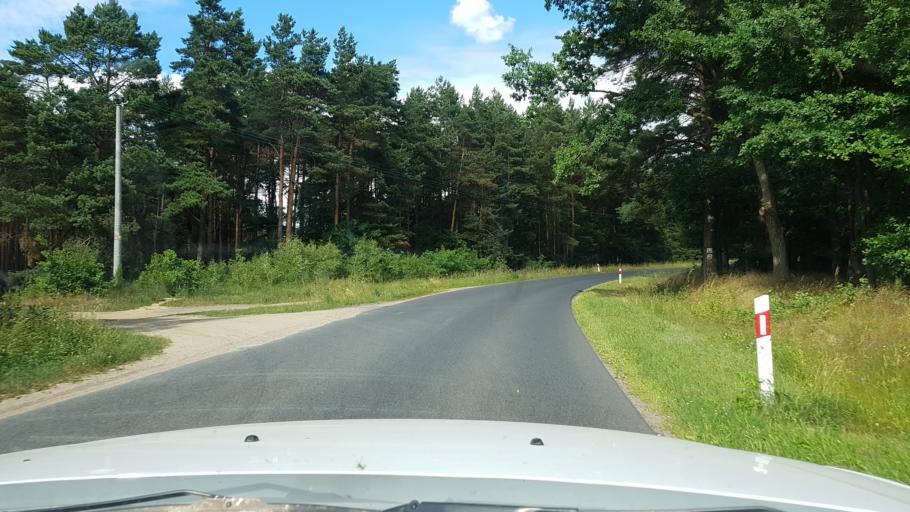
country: PL
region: West Pomeranian Voivodeship
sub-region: Powiat walecki
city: Miroslawiec
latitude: 53.4051
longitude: 15.9843
